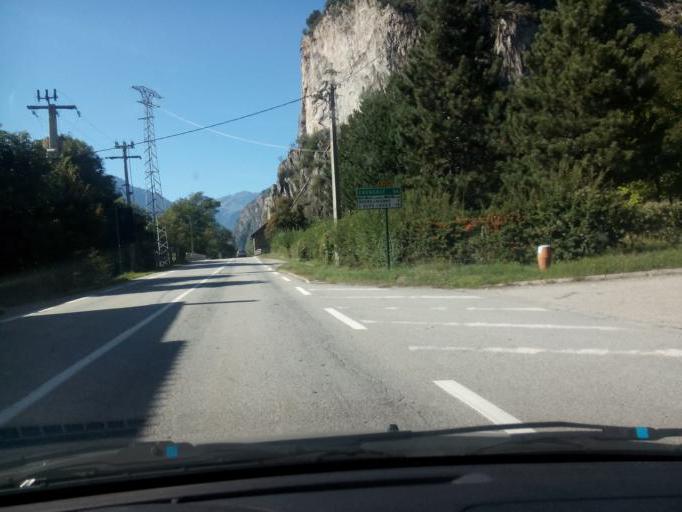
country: FR
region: Rhone-Alpes
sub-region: Departement de l'Isere
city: Huez
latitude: 45.0288
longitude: 6.0708
